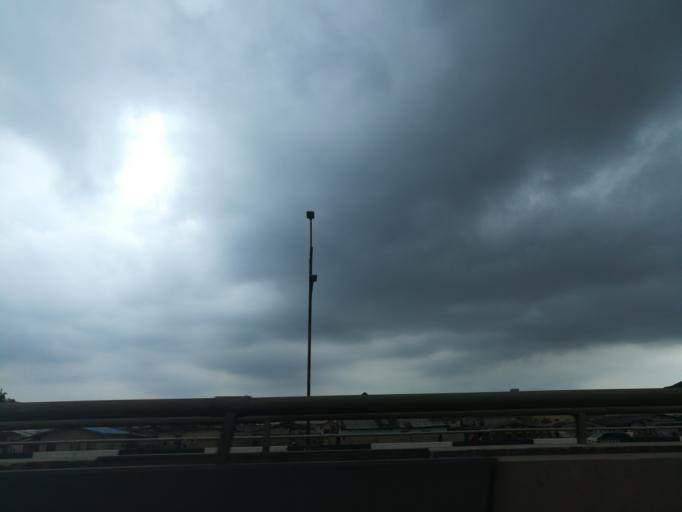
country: NG
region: Lagos
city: Somolu
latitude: 6.5424
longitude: 3.3993
